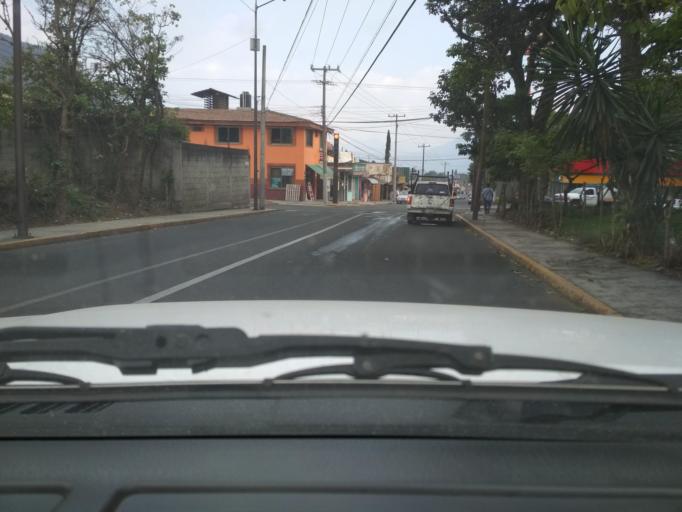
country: MX
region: Veracruz
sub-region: Mariano Escobedo
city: Palmira
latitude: 18.8708
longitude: -97.1021
